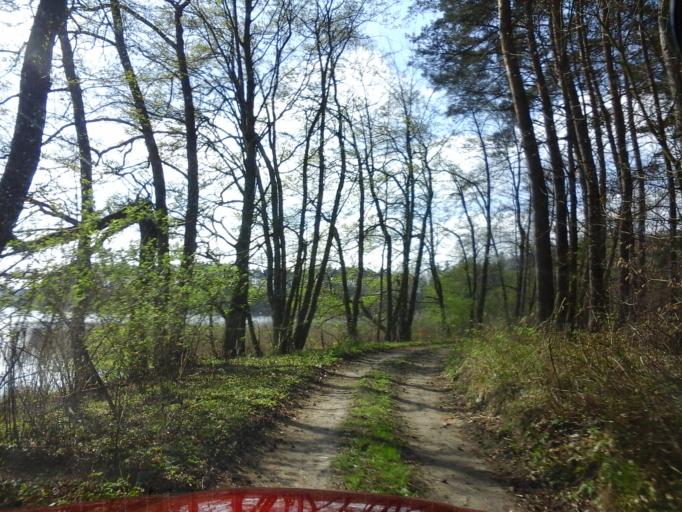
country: PL
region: West Pomeranian Voivodeship
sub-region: Powiat choszczenski
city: Bierzwnik
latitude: 53.0387
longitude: 15.5991
